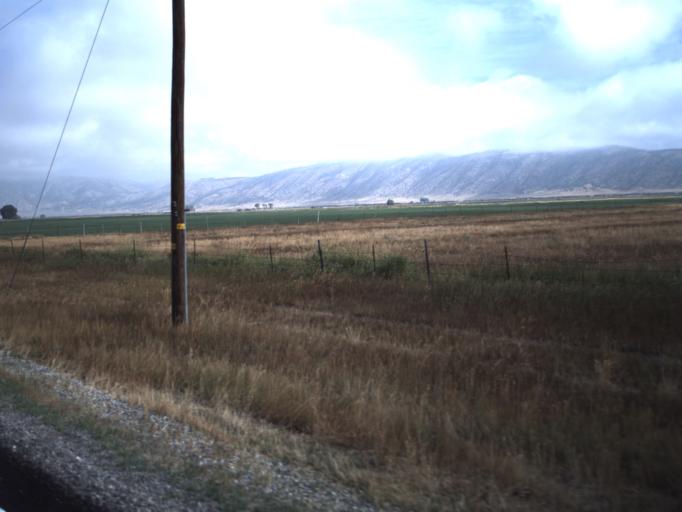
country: US
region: Utah
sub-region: Rich County
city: Randolph
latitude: 41.5315
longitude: -111.1629
